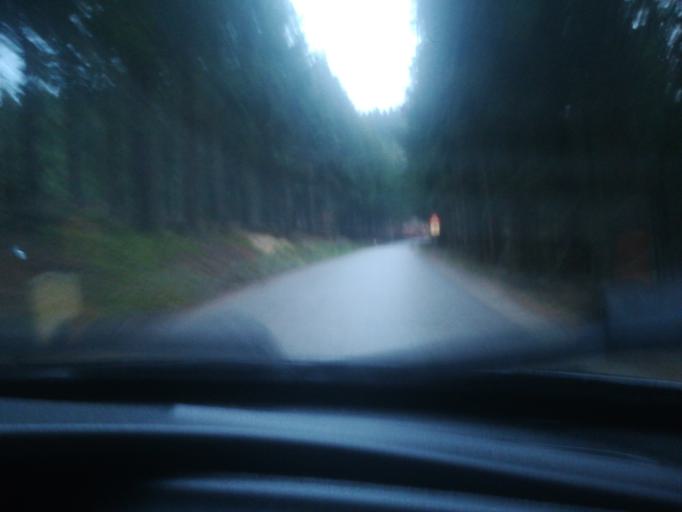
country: AT
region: Upper Austria
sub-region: Politischer Bezirk Perg
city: Perg
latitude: 48.3044
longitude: 14.6332
